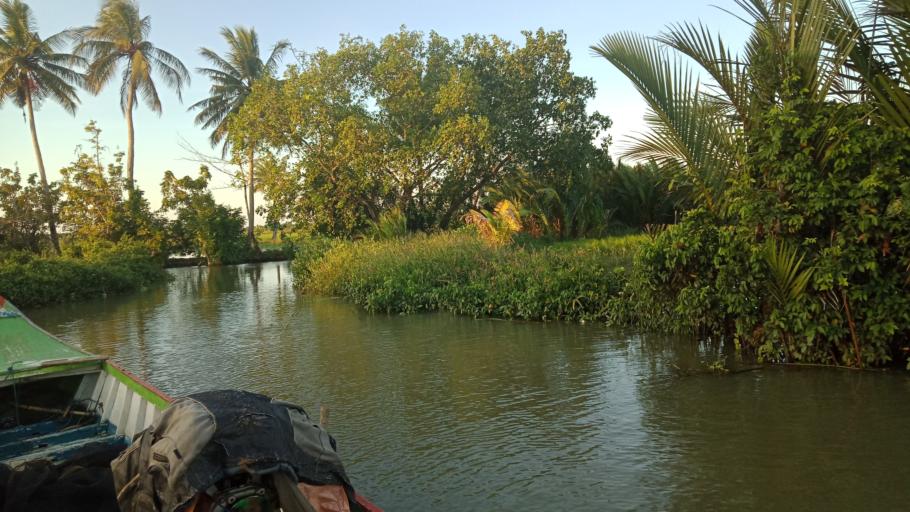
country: ID
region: South Sulawesi
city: Palakka
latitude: -4.3609
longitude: 120.3273
